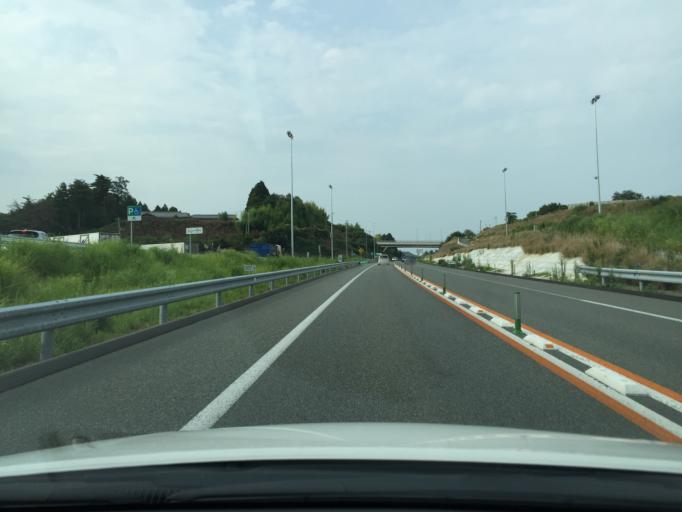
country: JP
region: Fukushima
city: Namie
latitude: 37.2863
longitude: 140.9816
